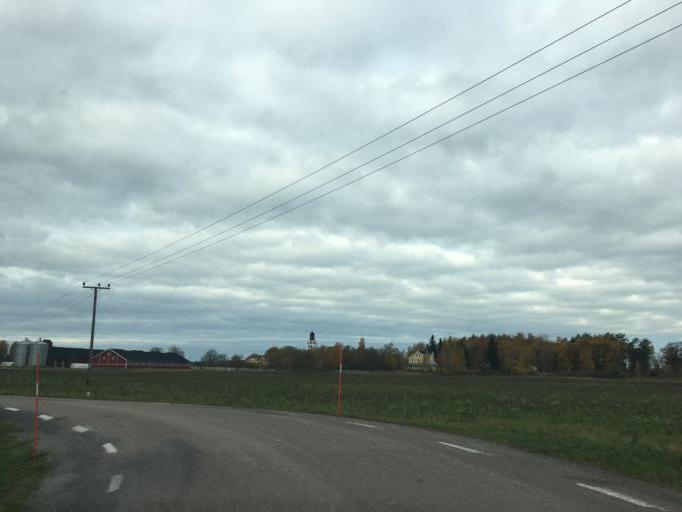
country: SE
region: Soedermanland
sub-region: Eskilstuna Kommun
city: Kvicksund
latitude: 59.5666
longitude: 16.4115
